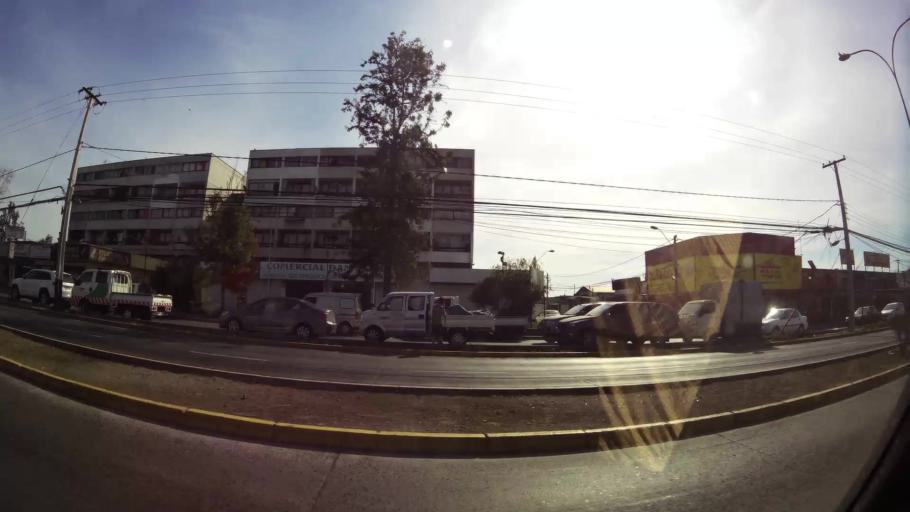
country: CL
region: Santiago Metropolitan
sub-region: Provincia de Santiago
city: La Pintana
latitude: -33.5351
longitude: -70.6345
